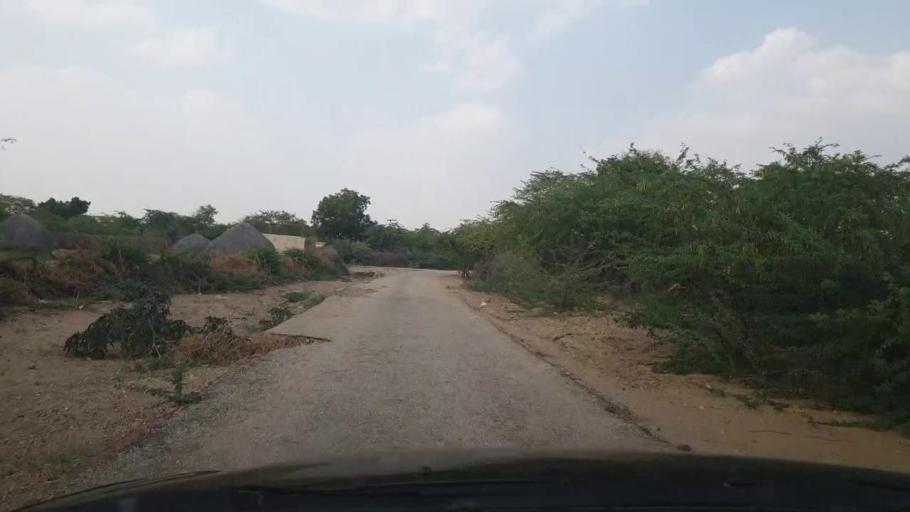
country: PK
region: Sindh
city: Islamkot
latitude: 24.9905
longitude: 70.5775
